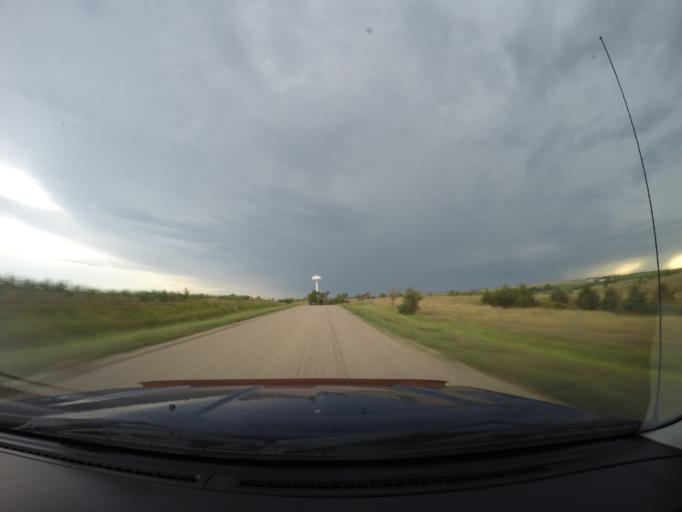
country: US
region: Nebraska
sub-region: Buffalo County
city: Kearney
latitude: 40.8418
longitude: -99.2614
